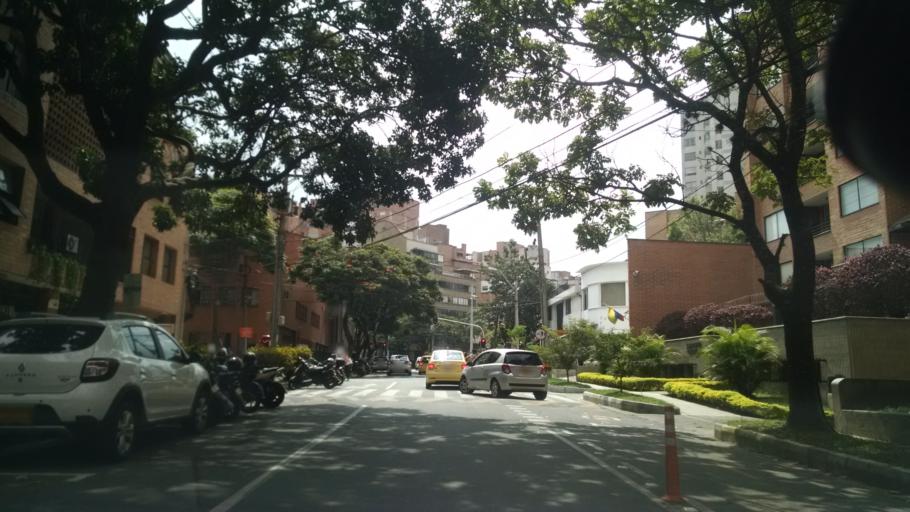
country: CO
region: Antioquia
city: Medellin
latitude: 6.2414
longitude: -75.5961
